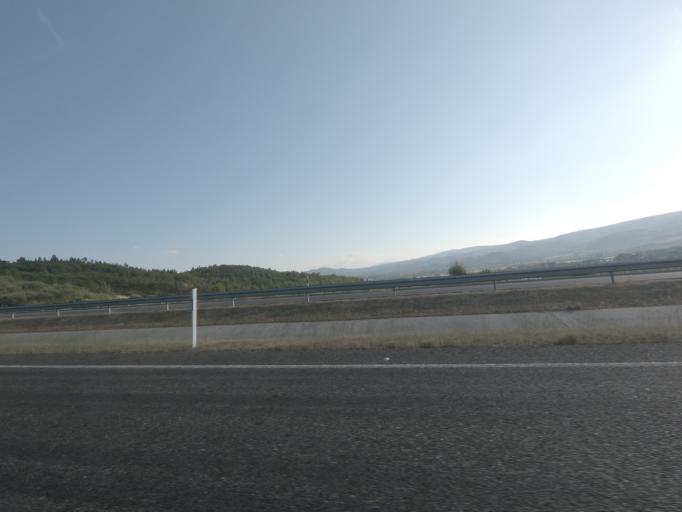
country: ES
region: Galicia
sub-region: Provincia de Ourense
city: Oimbra
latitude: 41.8627
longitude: -7.4271
